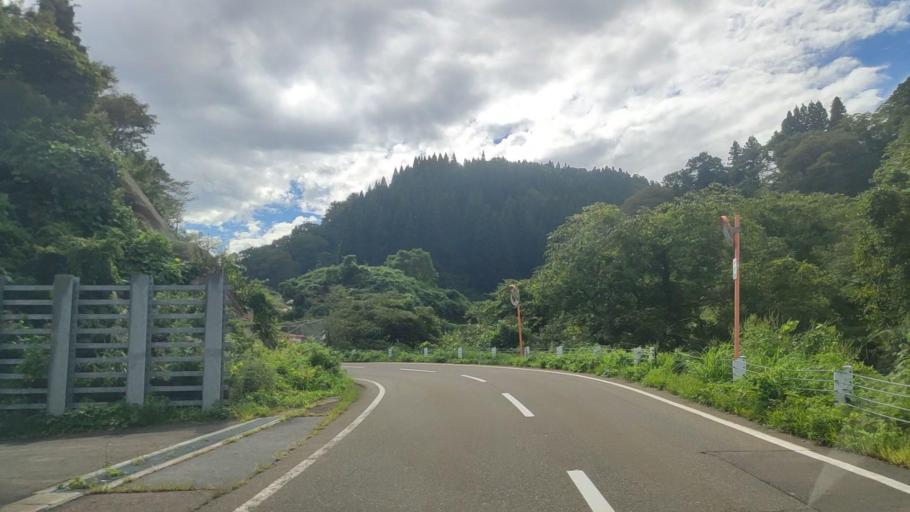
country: JP
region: Niigata
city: Arai
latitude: 36.9363
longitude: 138.2942
